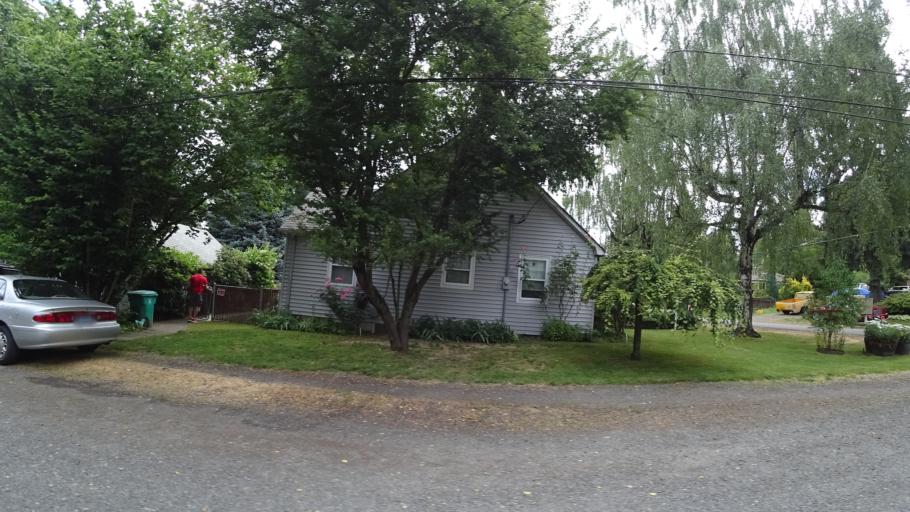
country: US
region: Oregon
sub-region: Multnomah County
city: Portland
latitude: 45.5653
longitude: -122.6117
